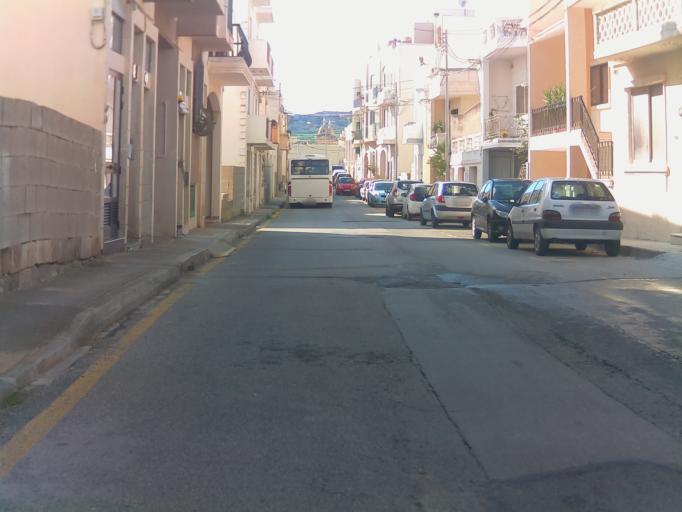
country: MT
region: L-Imgarr
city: Imgarr
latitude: 35.9232
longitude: 14.3671
